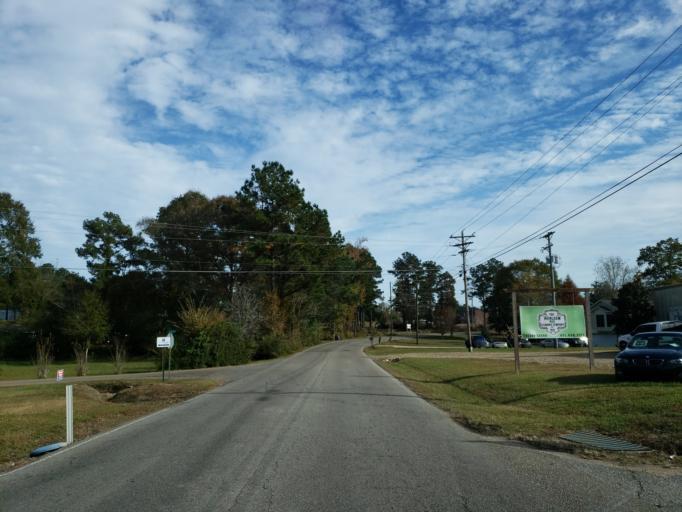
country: US
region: Mississippi
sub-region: Lamar County
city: West Hattiesburg
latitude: 31.3031
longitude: -89.3802
